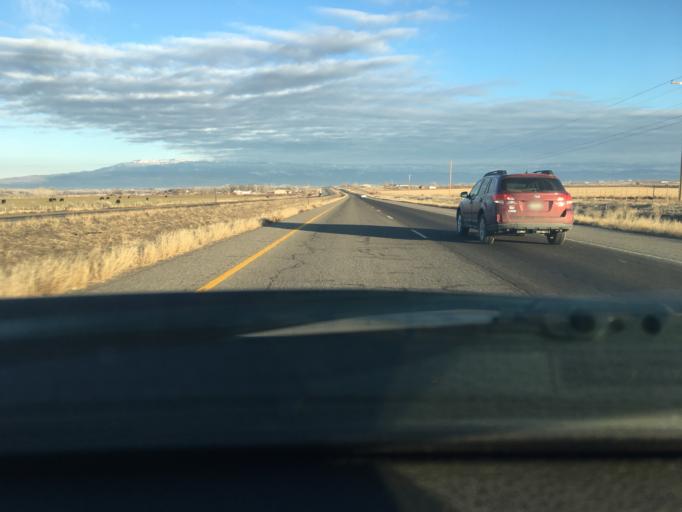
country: US
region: Colorado
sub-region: Montrose County
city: Olathe
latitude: 38.6407
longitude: -107.9878
